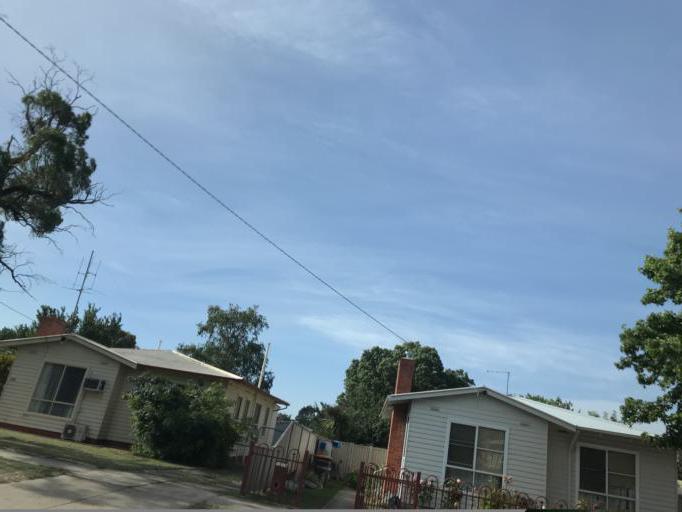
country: AU
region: Victoria
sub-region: Ballarat North
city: Newington
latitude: -37.5263
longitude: 143.8227
